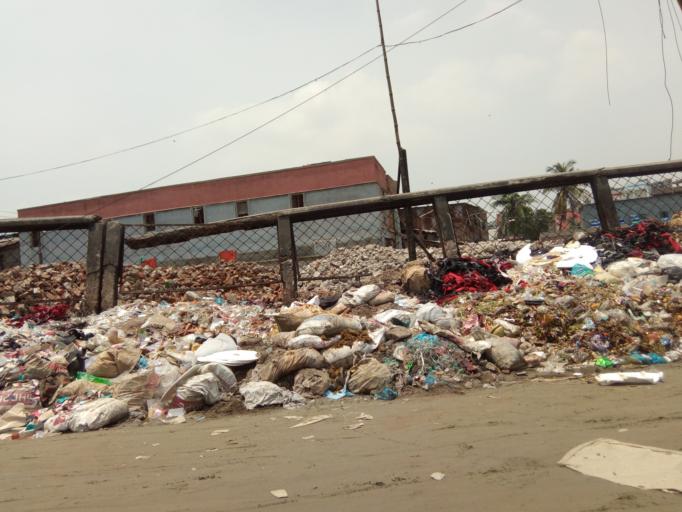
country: BD
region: Dhaka
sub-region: Dhaka
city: Dhaka
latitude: 23.7114
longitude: 90.3938
